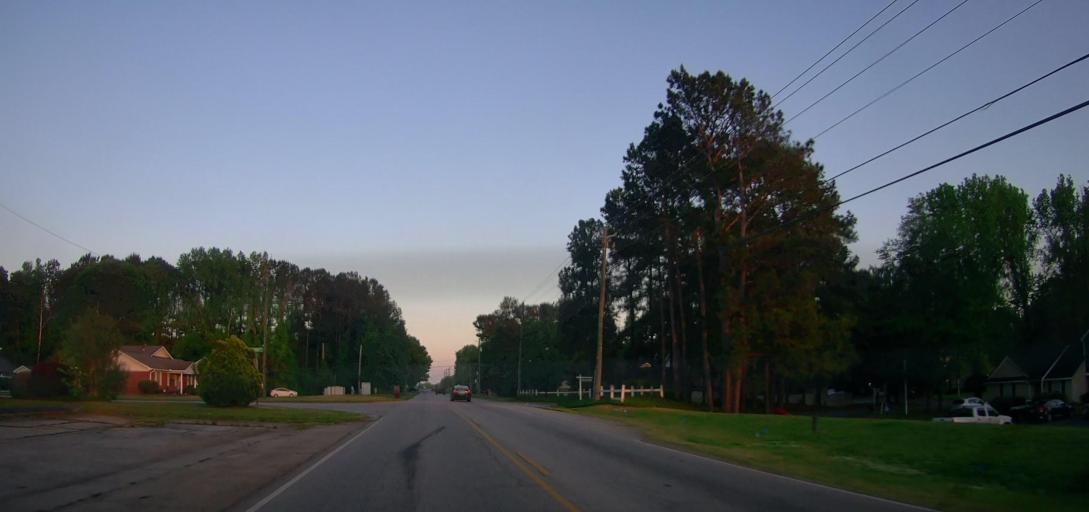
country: US
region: Georgia
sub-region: Henry County
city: McDonough
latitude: 33.4362
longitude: -84.1852
